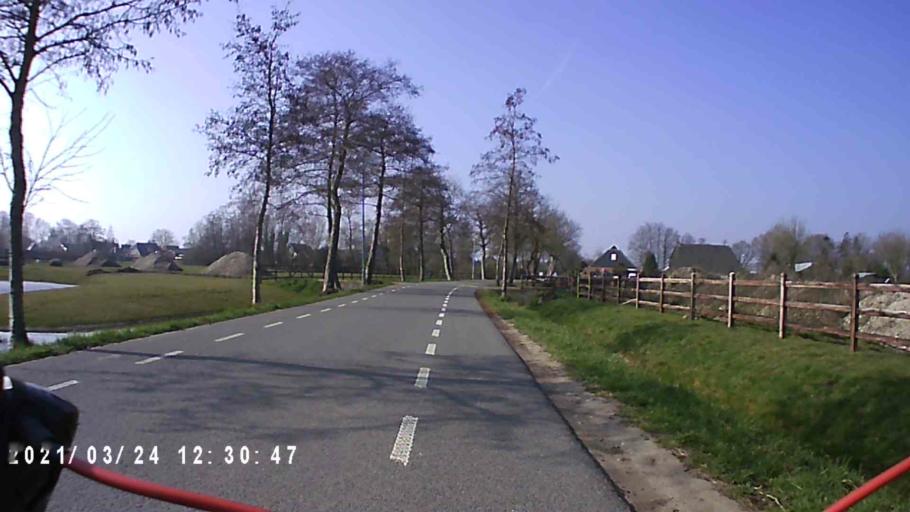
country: NL
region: Groningen
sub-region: Gemeente Leek
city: Leek
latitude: 53.1747
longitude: 6.3661
